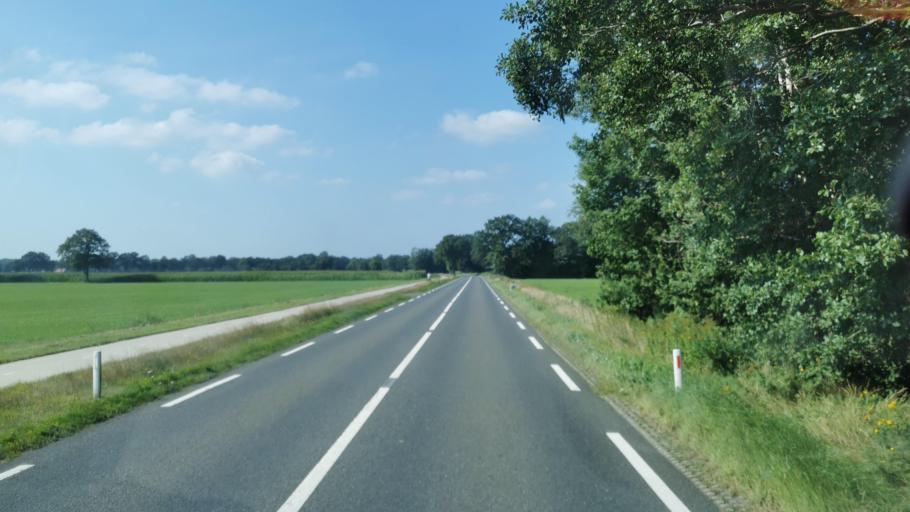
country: NL
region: Overijssel
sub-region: Gemeente Oldenzaal
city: Oldenzaal
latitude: 52.3720
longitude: 6.9075
